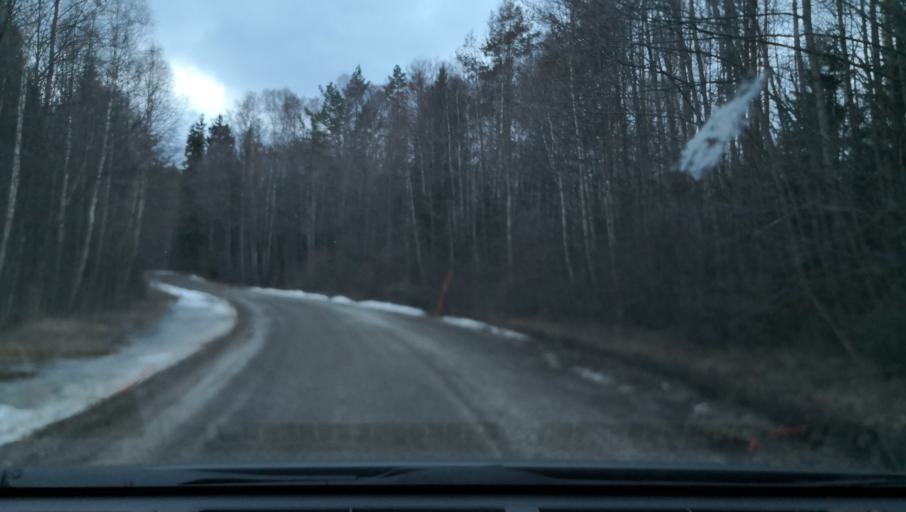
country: SE
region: Vaestmanland
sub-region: Kopings Kommun
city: Kolsva
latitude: 59.6025
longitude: 15.6535
